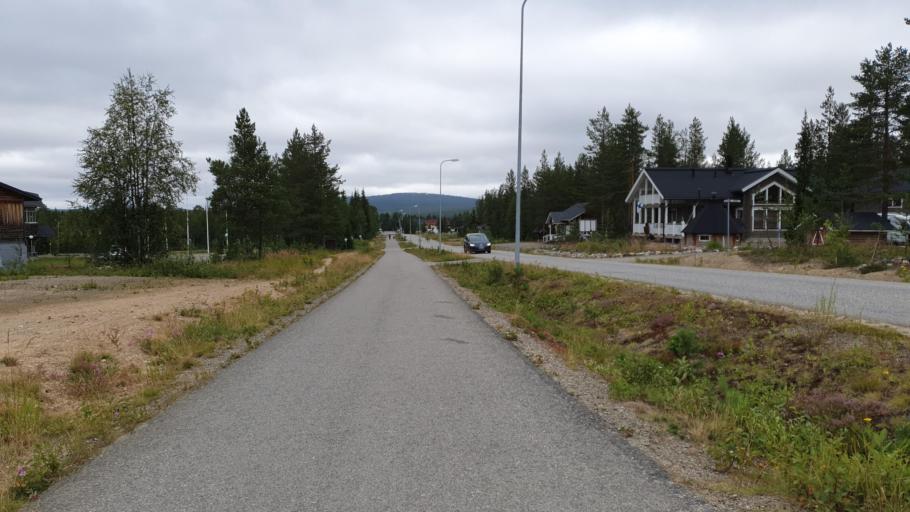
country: FI
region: Lapland
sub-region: Tunturi-Lappi
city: Kolari
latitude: 67.5990
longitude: 24.1514
